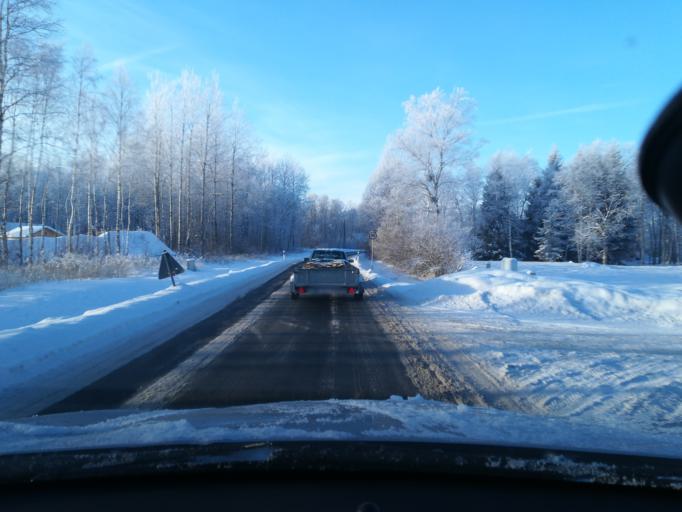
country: EE
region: Harju
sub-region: Saue linn
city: Saue
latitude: 59.3730
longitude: 24.5433
